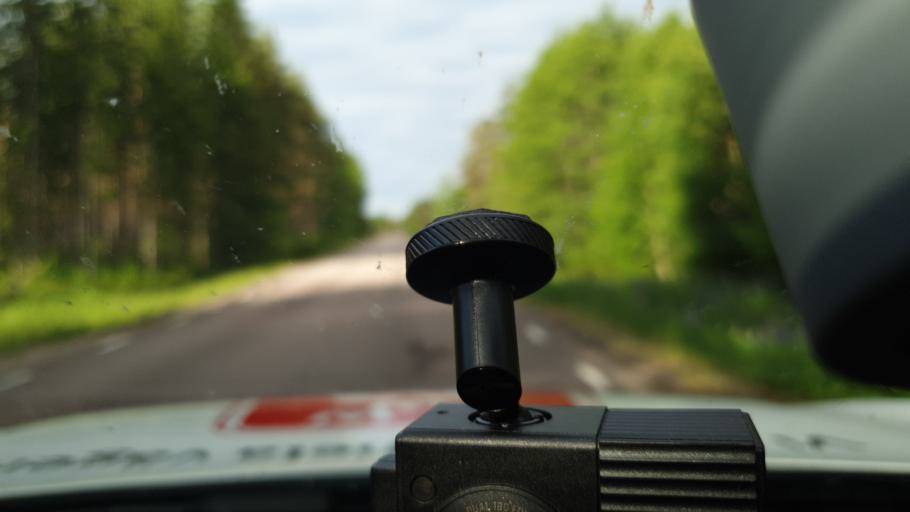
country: SE
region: Vaermland
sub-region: Torsby Kommun
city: Torsby
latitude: 60.1061
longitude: 12.9062
